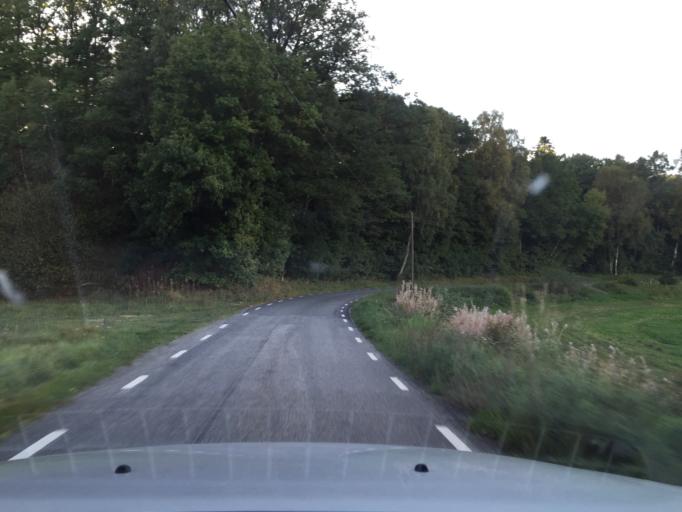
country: SE
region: Skane
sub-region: Hassleholms Kommun
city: Sosdala
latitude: 55.9871
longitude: 13.7336
